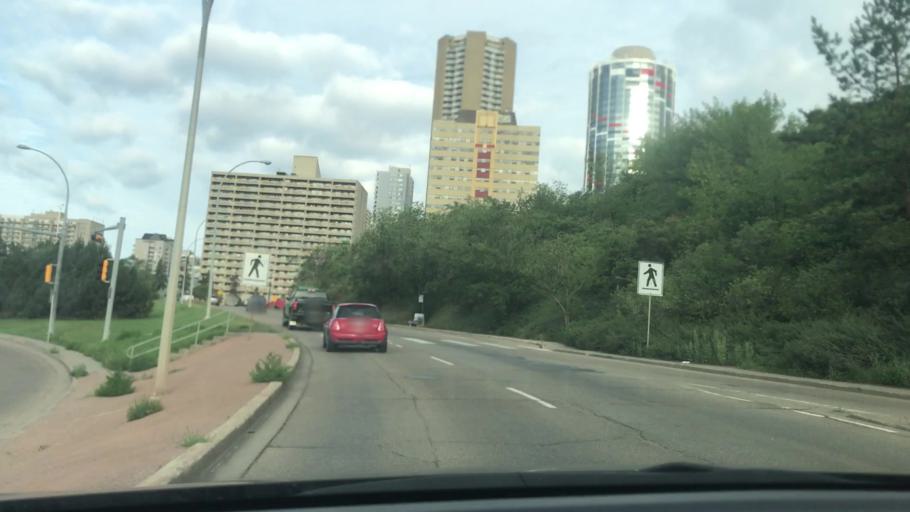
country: CA
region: Alberta
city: Edmonton
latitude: 53.5387
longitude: -113.4897
